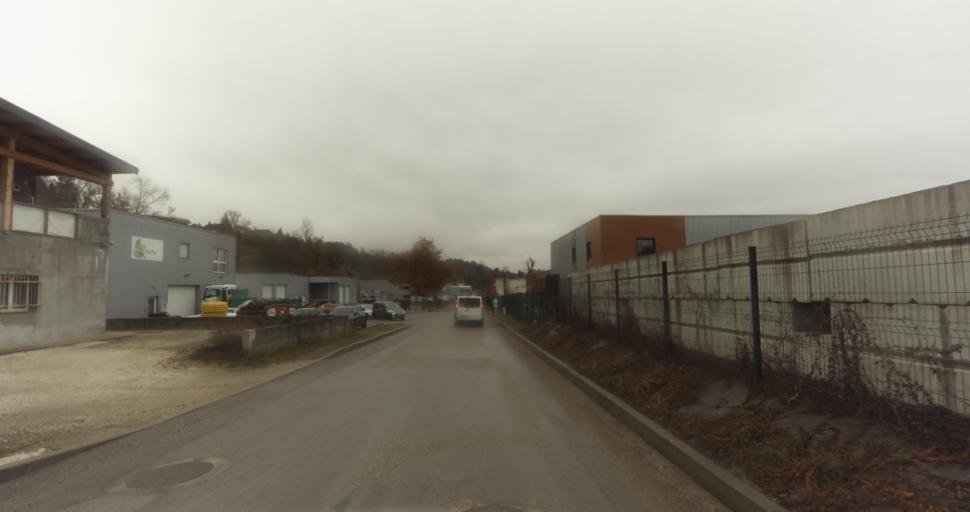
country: FR
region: Rhone-Alpes
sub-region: Departement de la Haute-Savoie
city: Saint-Martin-Bellevue
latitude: 45.9583
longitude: 6.1697
